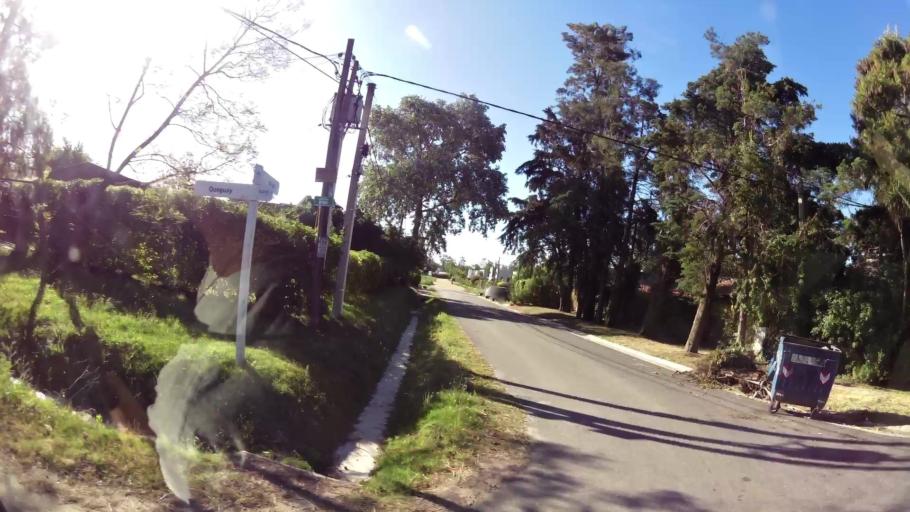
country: UY
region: Canelones
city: Barra de Carrasco
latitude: -34.8609
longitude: -56.0320
